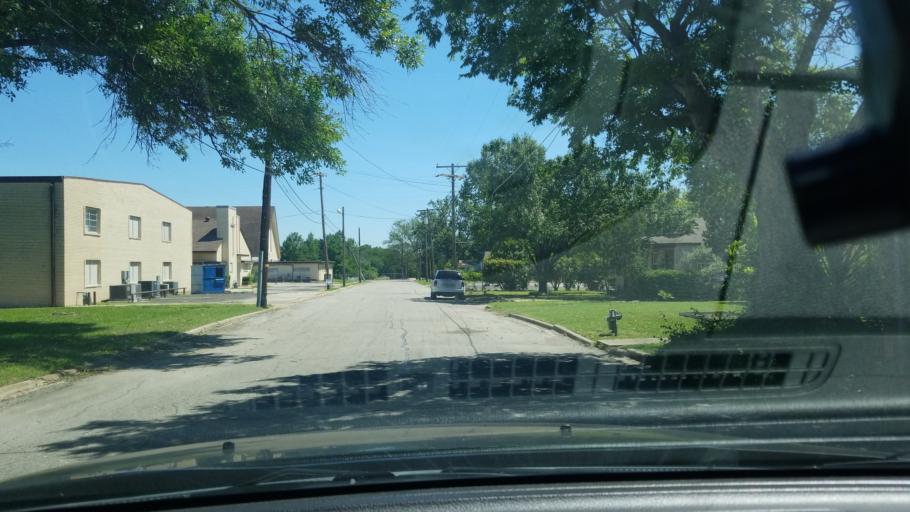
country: US
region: Texas
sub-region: Dallas County
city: Mesquite
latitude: 32.7641
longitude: -96.6024
